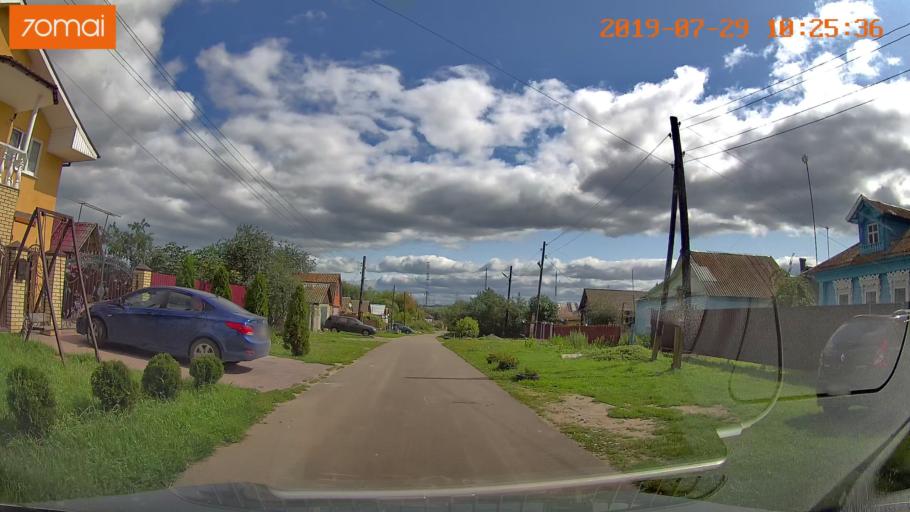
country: RU
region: Moskovskaya
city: Voskresensk
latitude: 55.2969
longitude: 38.6633
